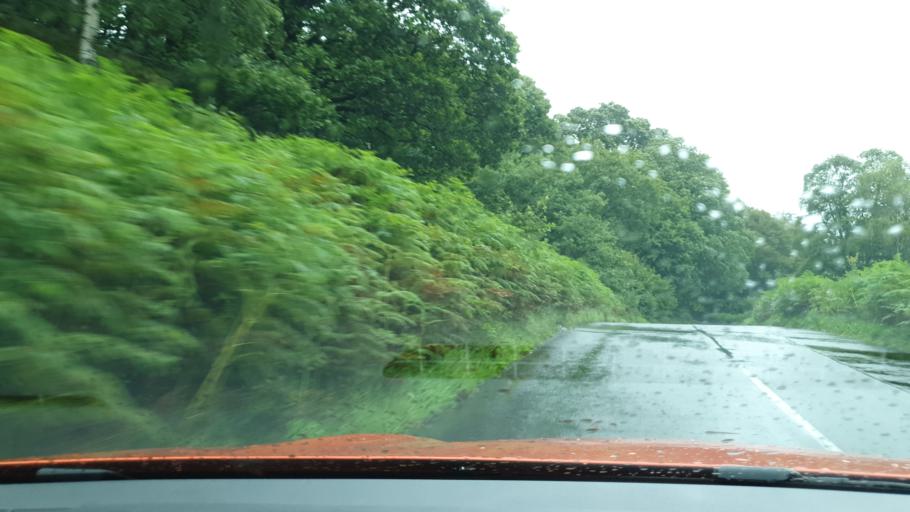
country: GB
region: England
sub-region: Cumbria
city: Ulverston
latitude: 54.3045
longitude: -3.0976
